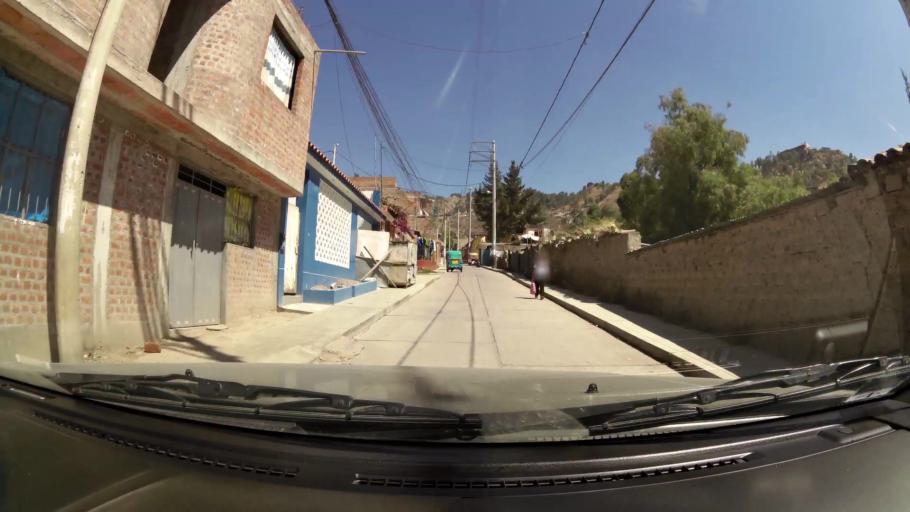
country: PE
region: Ayacucho
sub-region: Provincia de Huamanga
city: Ayacucho
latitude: -13.1682
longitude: -74.2335
